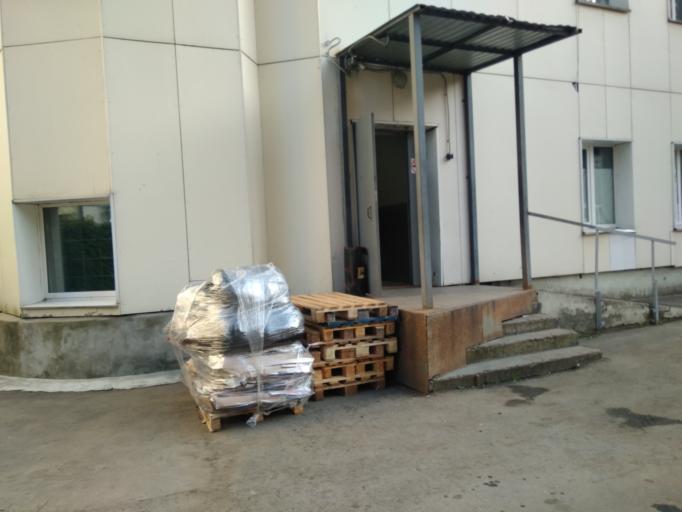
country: RU
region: Moskovskaya
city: Zhukovskiy
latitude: 55.5837
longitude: 38.1374
